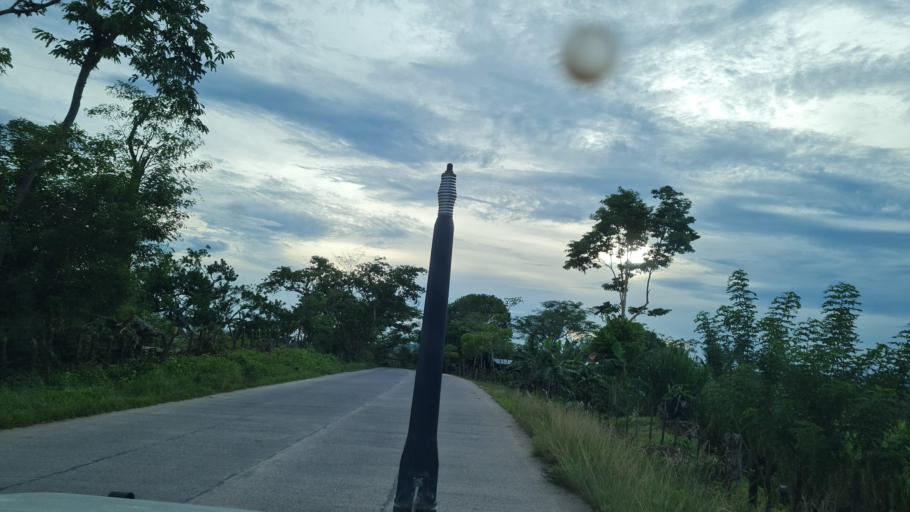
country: NI
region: Atlantico Norte (RAAN)
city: Siuna
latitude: 13.6839
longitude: -84.5913
